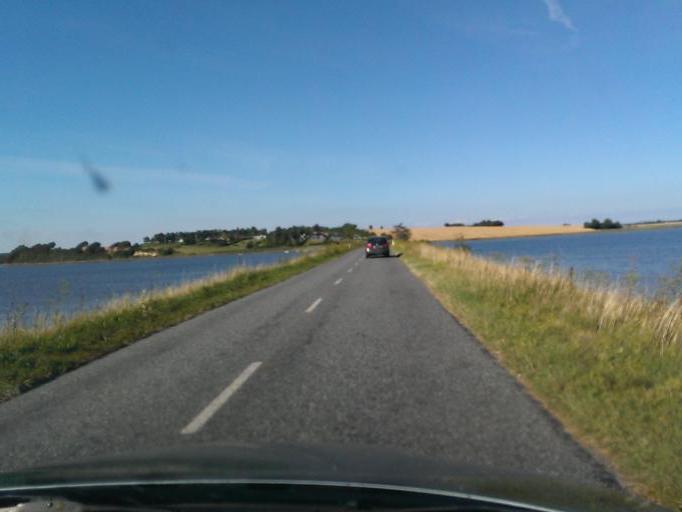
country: DK
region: Central Jutland
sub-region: Odder Kommune
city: Odder
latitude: 55.8659
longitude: 10.1164
